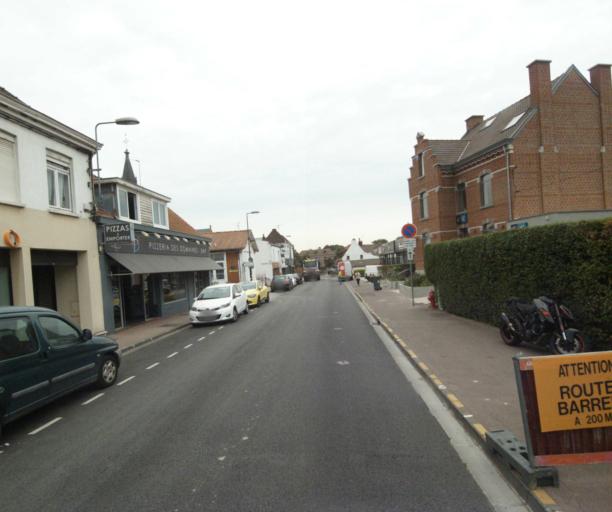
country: FR
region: Nord-Pas-de-Calais
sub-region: Departement du Nord
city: Bondues
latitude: 50.7028
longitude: 3.0930
